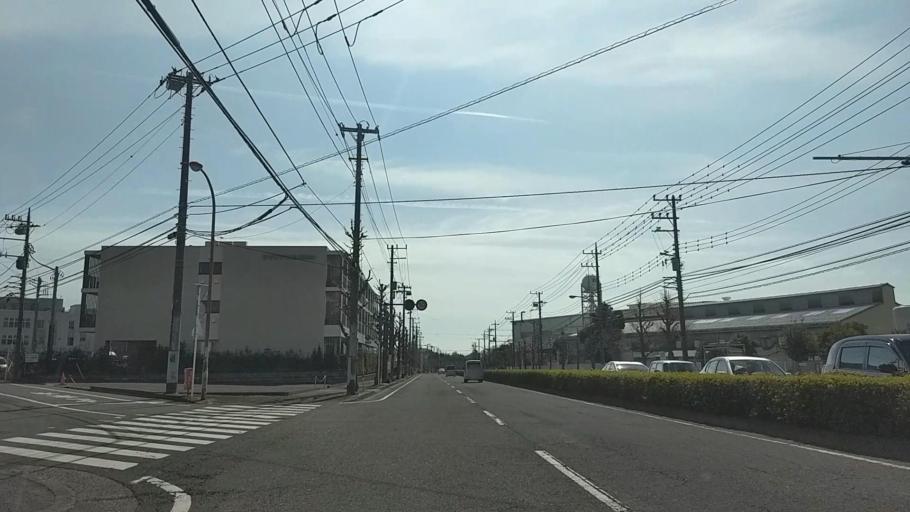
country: JP
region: Kanagawa
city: Fujisawa
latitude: 35.3890
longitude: 139.4575
